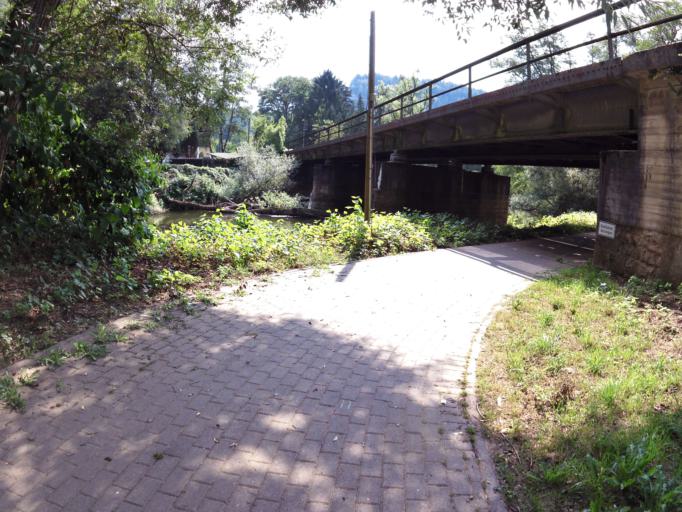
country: DE
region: Rheinland-Pfalz
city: Kordel
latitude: 49.8250
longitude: 6.6493
